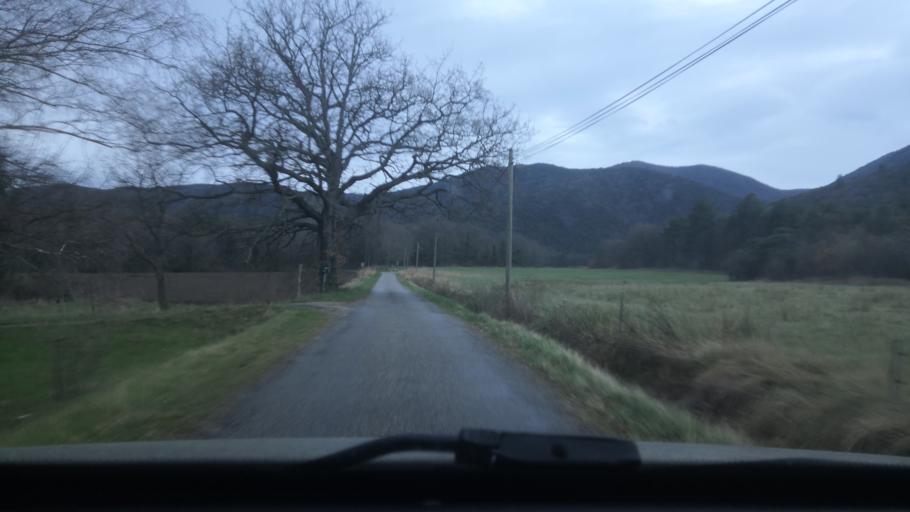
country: FR
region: Rhone-Alpes
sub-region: Departement de la Drome
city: Dieulefit
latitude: 44.5231
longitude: 5.0227
